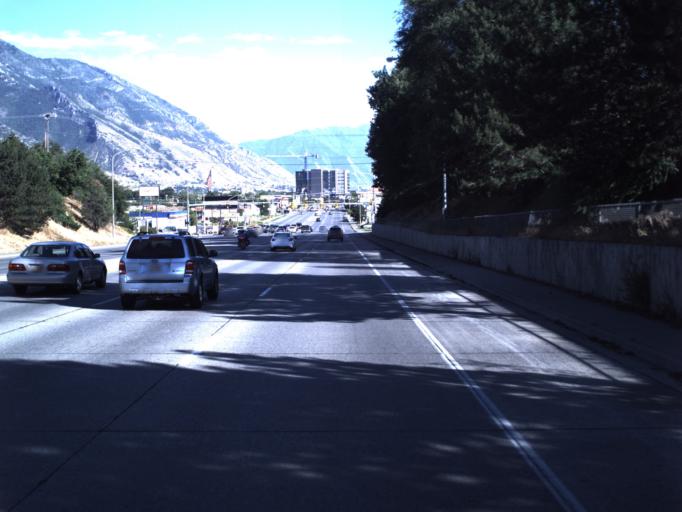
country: US
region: Utah
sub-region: Utah County
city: Provo
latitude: 40.2580
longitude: -111.6740
